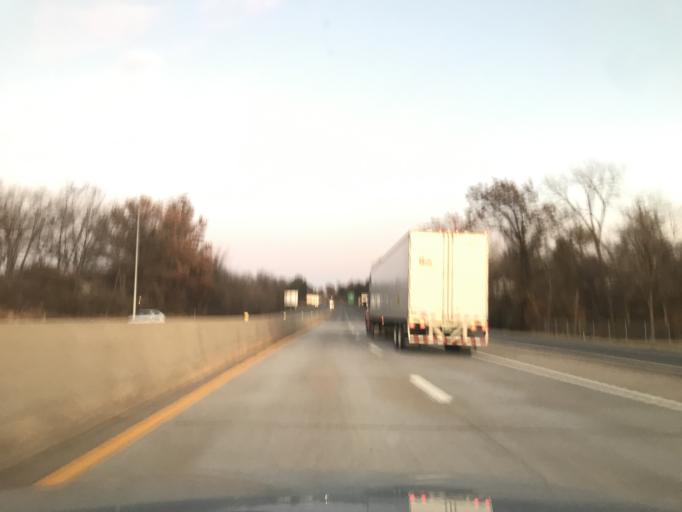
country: US
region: Missouri
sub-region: Marion County
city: Hannibal
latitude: 39.7148
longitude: -91.3899
